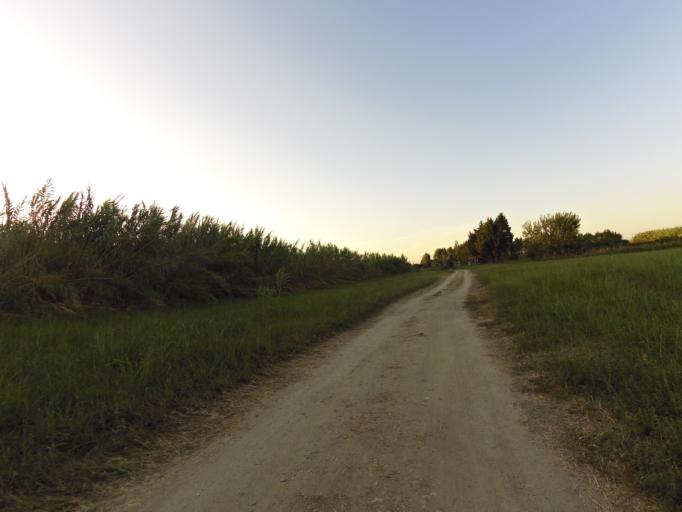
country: IT
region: Calabria
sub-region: Provincia di Reggio Calabria
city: Monasterace Marina
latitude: 38.4502
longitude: 16.5800
